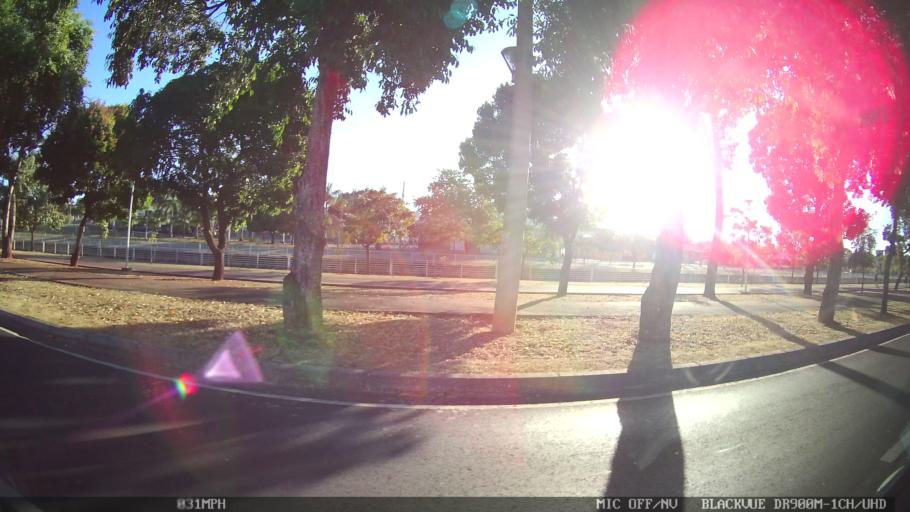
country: BR
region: Sao Paulo
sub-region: Sao Jose Do Rio Preto
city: Sao Jose do Rio Preto
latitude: -20.7911
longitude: -49.3762
